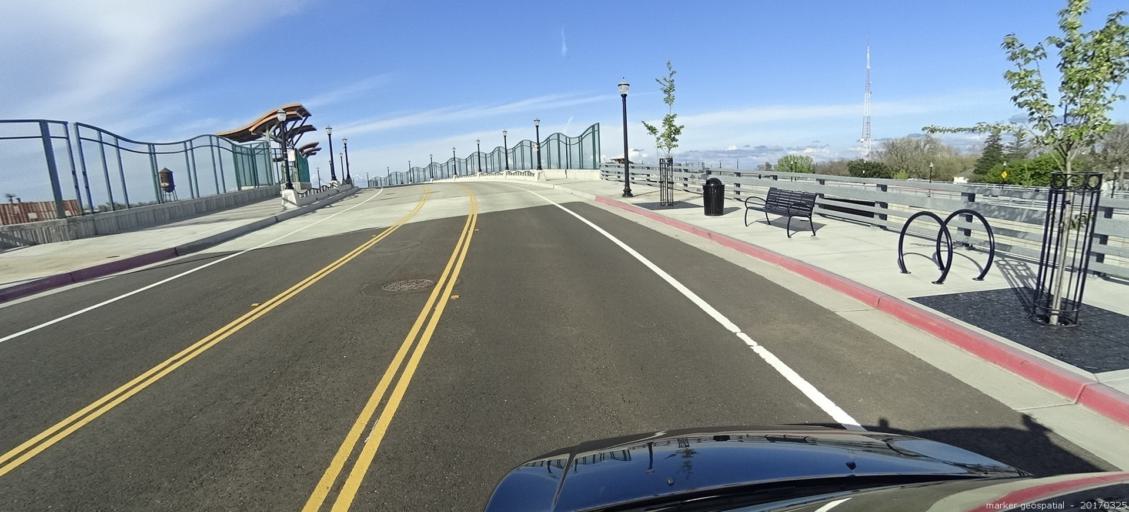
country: US
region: California
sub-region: Sacramento County
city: Sacramento
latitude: 38.5858
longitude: -121.4981
